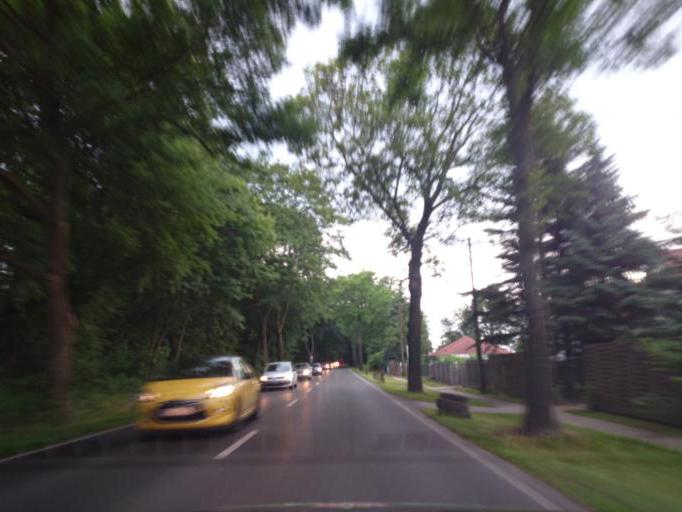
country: DE
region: Berlin
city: Hellersdorf
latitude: 52.5433
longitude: 13.6301
